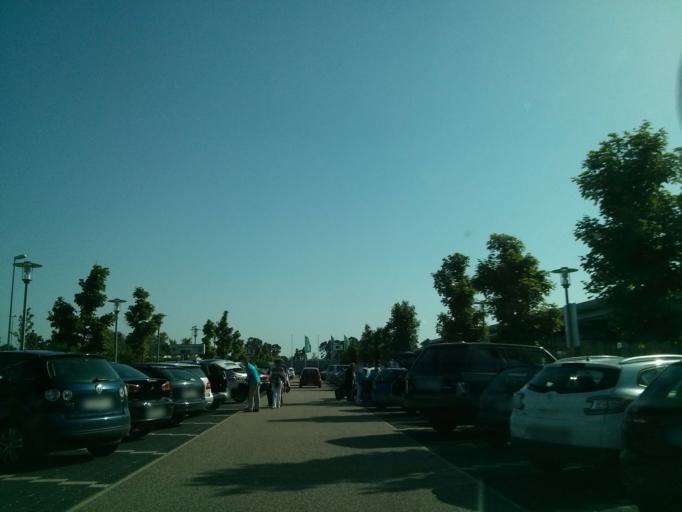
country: DE
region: Baden-Wuerttemberg
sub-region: Karlsruhe Region
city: Hugelsheim
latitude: 48.7784
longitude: 8.0886
